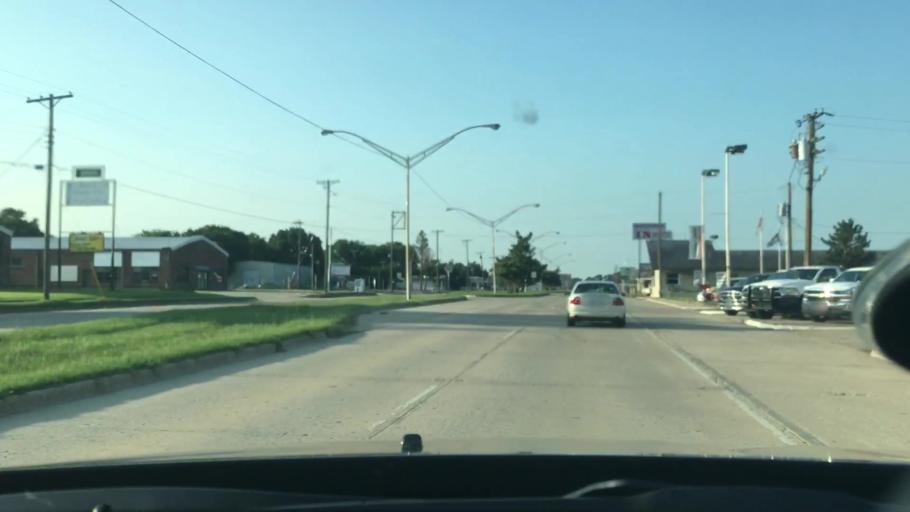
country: US
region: Oklahoma
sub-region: Pontotoc County
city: Ada
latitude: 34.7855
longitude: -96.6788
